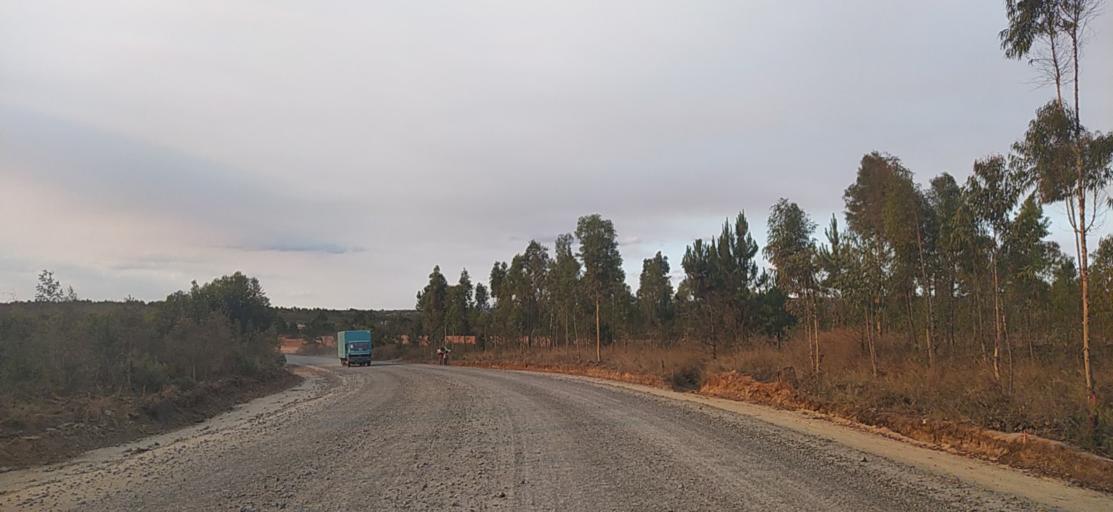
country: MG
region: Analamanga
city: Anjozorobe
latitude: -18.5027
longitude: 48.2679
